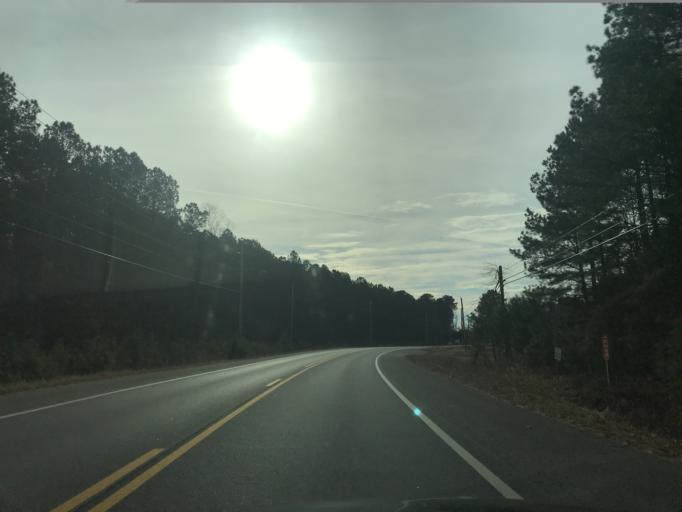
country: US
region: Maryland
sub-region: Charles County
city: Cobb Island
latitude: 38.3120
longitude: -76.8868
